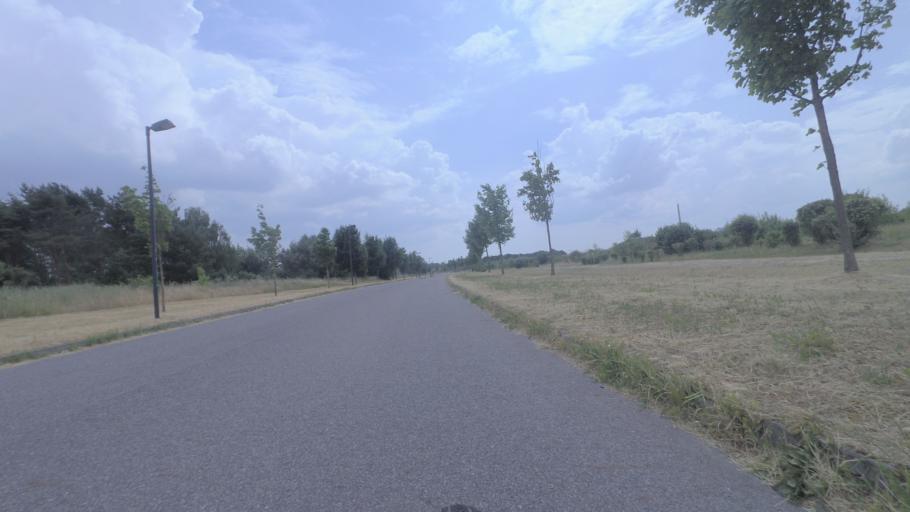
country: DE
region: Brandenburg
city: Grossbeeren
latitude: 52.3268
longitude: 13.2922
